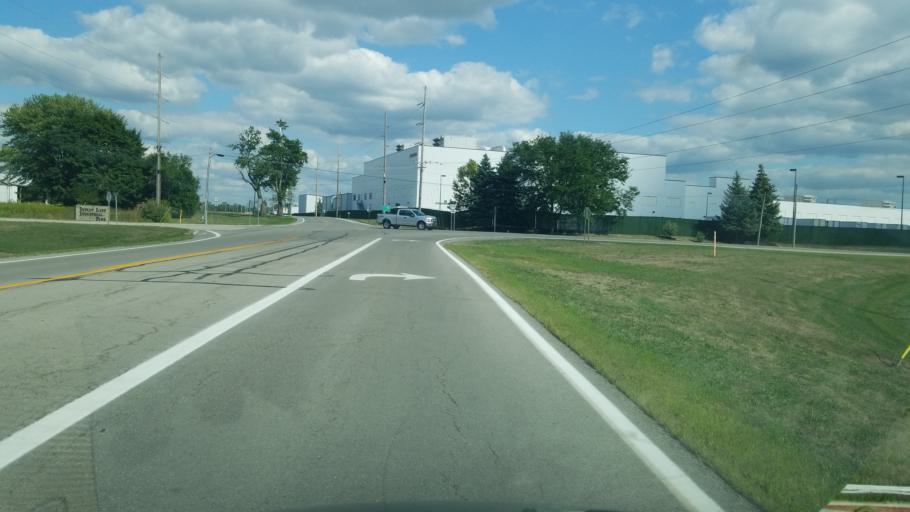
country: US
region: Ohio
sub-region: Logan County
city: Russells Point
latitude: 40.4506
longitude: -83.9045
